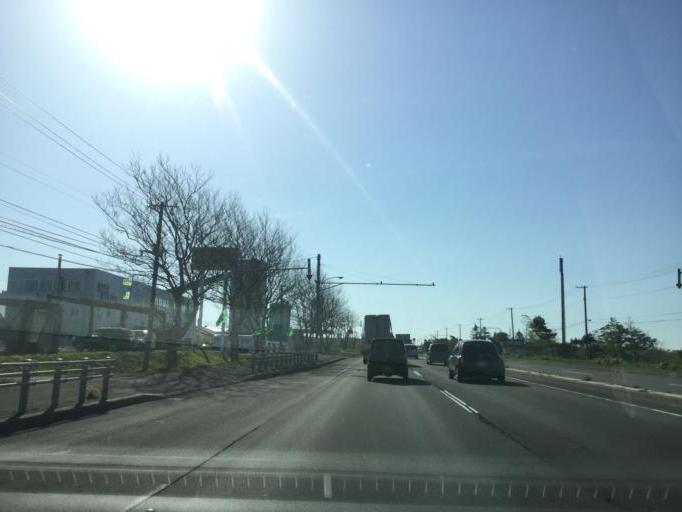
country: JP
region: Hokkaido
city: Kitahiroshima
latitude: 43.0122
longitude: 141.5081
